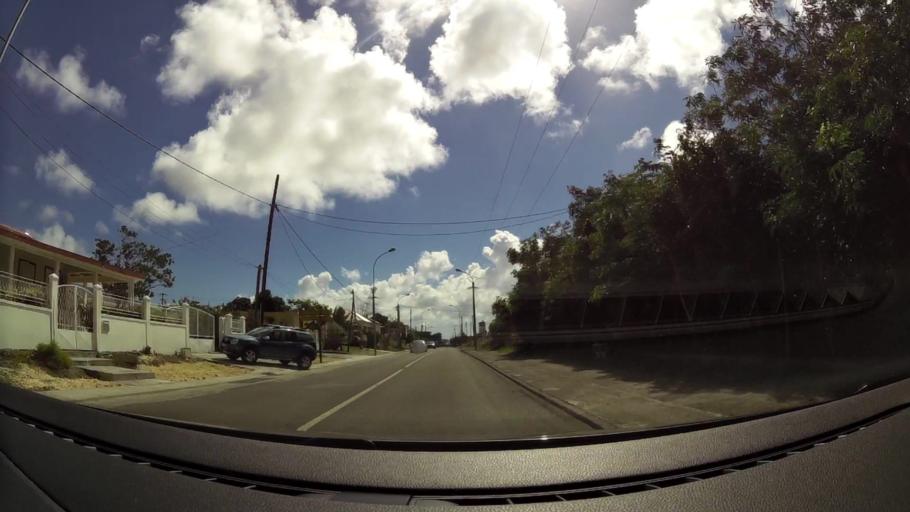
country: GP
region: Guadeloupe
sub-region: Guadeloupe
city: Petit-Canal
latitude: 16.4241
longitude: -61.4749
